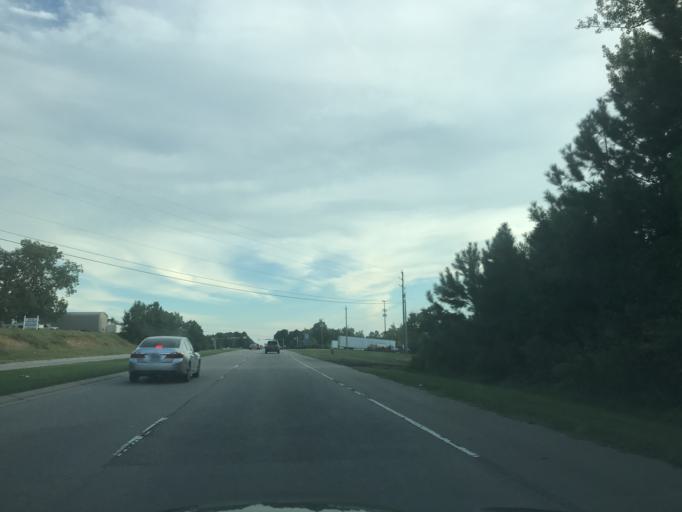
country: US
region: North Carolina
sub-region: Wake County
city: Green Level
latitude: 35.8062
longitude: -78.8718
